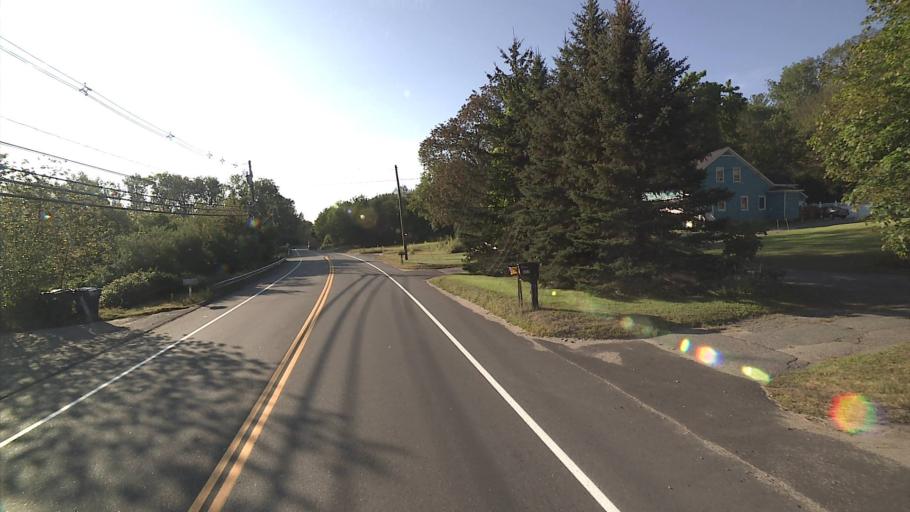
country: US
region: Connecticut
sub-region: Windham County
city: Willimantic
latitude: 41.7013
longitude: -72.1901
